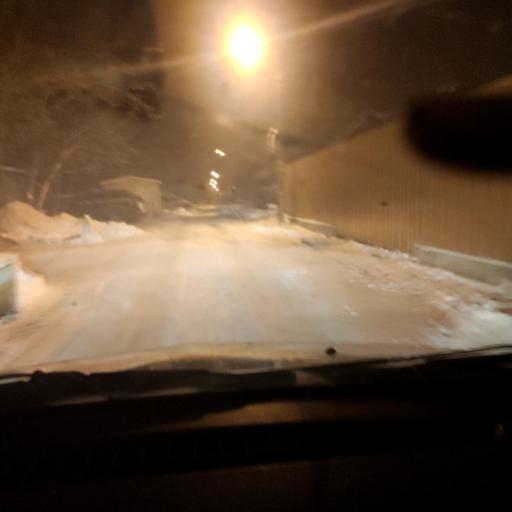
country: RU
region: Bashkortostan
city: Ufa
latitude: 54.7062
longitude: 55.9372
